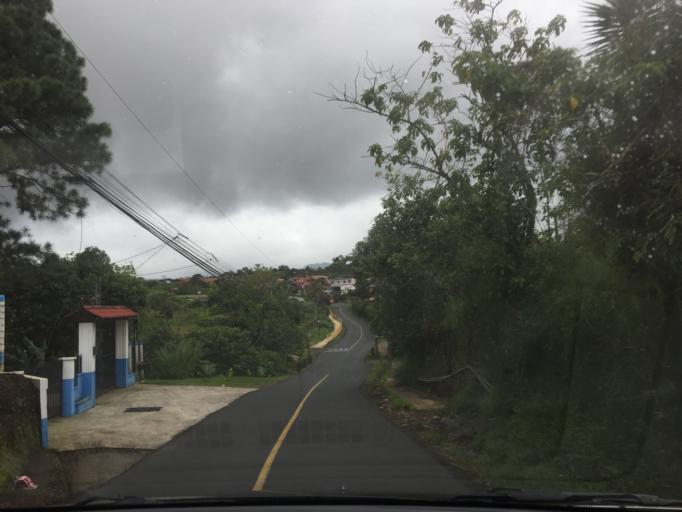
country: CR
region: Heredia
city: Angeles
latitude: 10.0181
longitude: -84.0349
